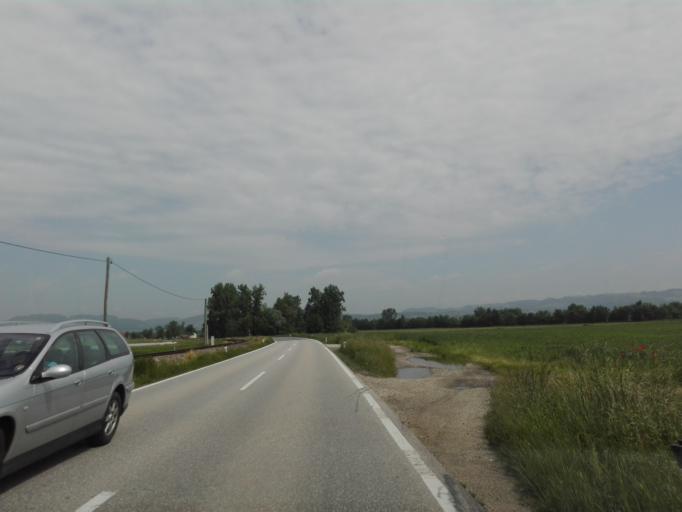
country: AT
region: Upper Austria
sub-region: Politischer Bezirk Urfahr-Umgebung
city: Feldkirchen an der Donau
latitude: 48.3429
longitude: 13.9984
